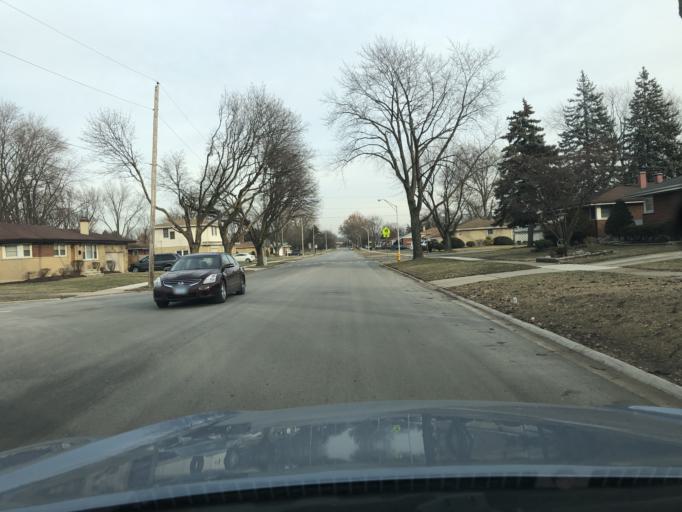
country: US
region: Illinois
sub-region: DuPage County
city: Addison
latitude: 41.9417
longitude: -87.9963
